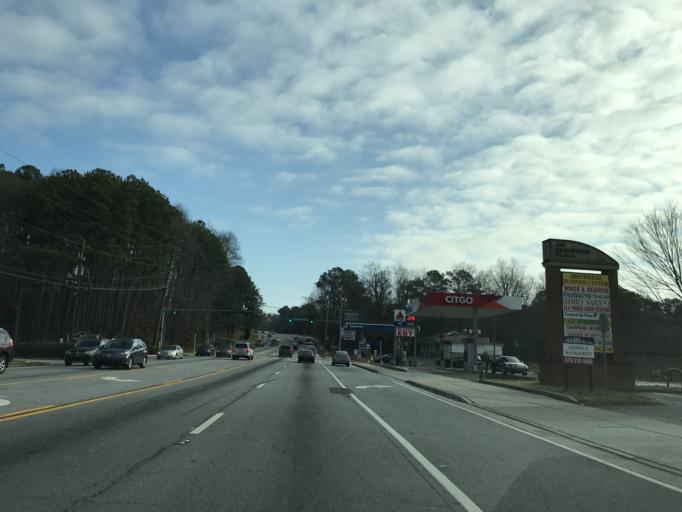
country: US
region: Georgia
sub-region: Clayton County
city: Riverdale
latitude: 33.5791
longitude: -84.3843
